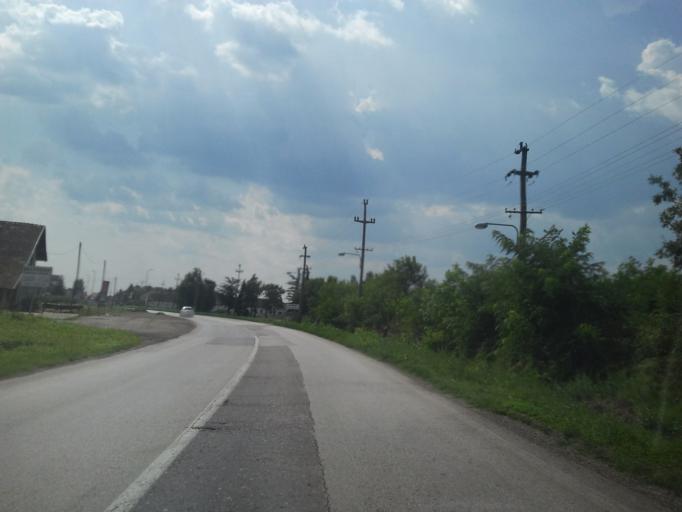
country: RS
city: Glozan
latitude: 45.2423
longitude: 19.6429
